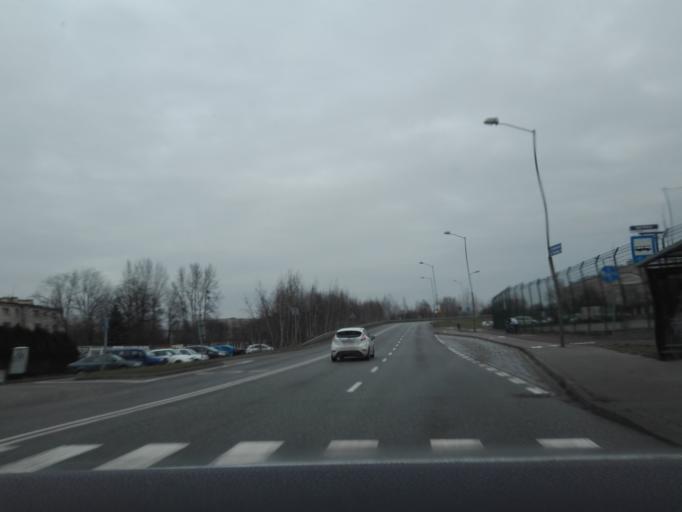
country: PL
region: Silesian Voivodeship
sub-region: Katowice
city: Katowice
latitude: 50.2707
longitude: 19.0157
